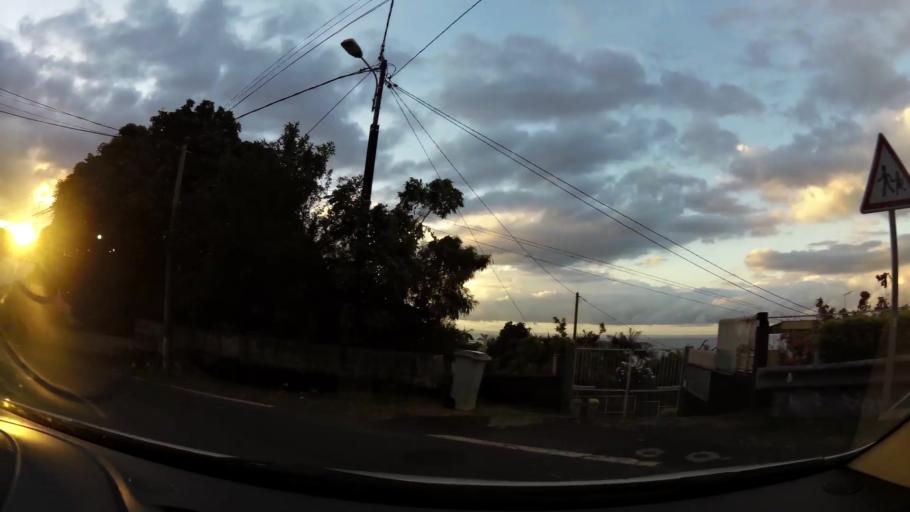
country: RE
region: Reunion
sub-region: Reunion
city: Saint-Denis
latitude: -20.9082
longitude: 55.4631
